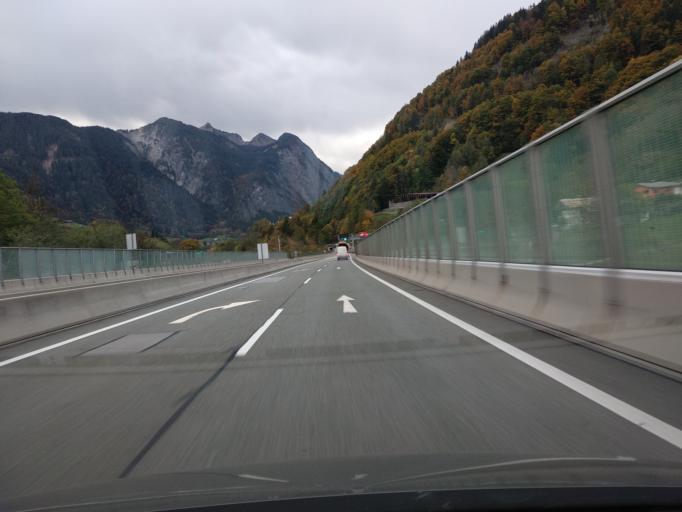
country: AT
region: Vorarlberg
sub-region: Politischer Bezirk Bludenz
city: Dalaas
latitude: 47.1246
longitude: 10.0122
